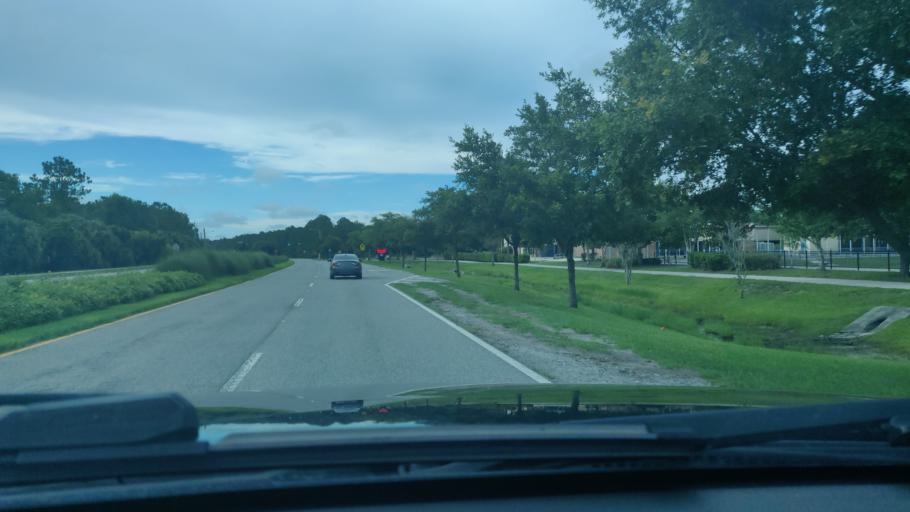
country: US
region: Florida
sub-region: Flagler County
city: Palm Coast
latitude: 29.5305
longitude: -81.2252
